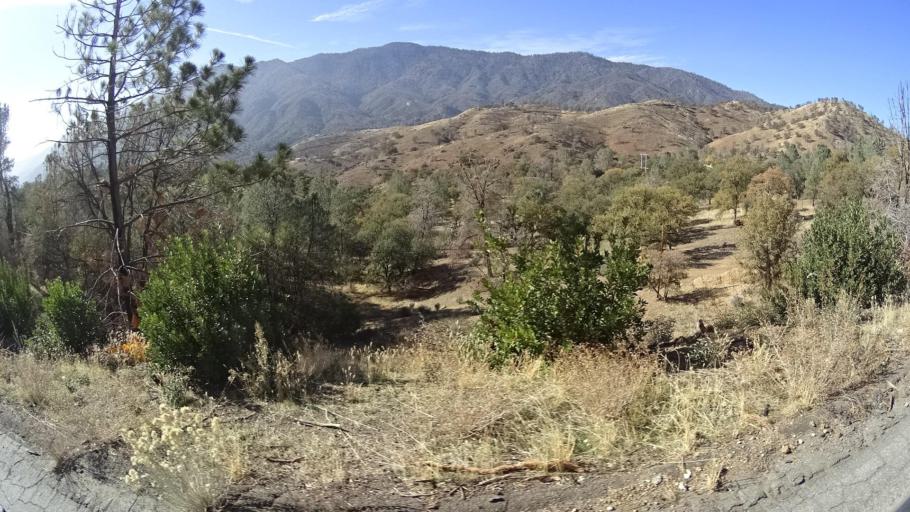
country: US
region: California
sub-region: Kern County
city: Bodfish
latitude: 35.4513
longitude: -118.5279
